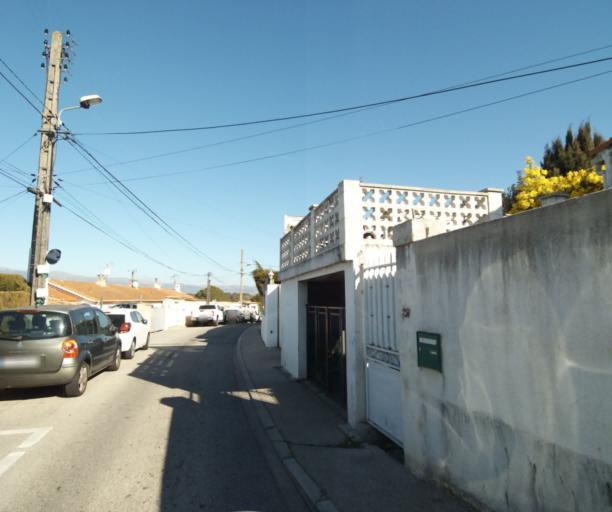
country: FR
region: Provence-Alpes-Cote d'Azur
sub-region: Departement des Alpes-Maritimes
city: Biot
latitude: 43.6064
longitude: 7.0851
